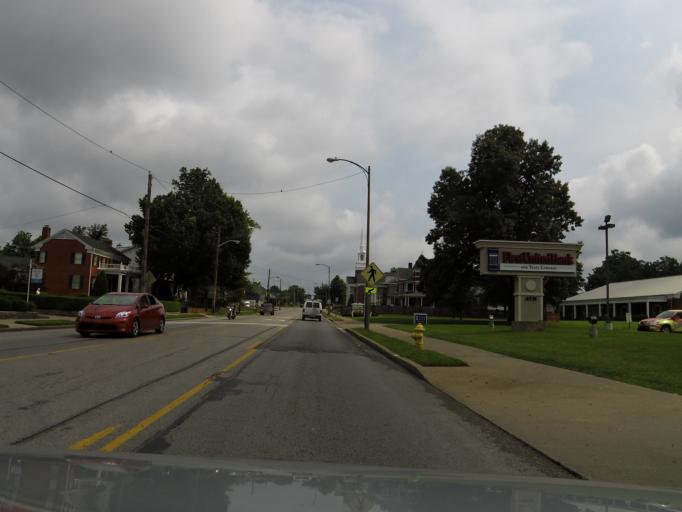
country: US
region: Kentucky
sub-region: Hopkins County
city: Madisonville
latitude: 37.3310
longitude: -87.4984
